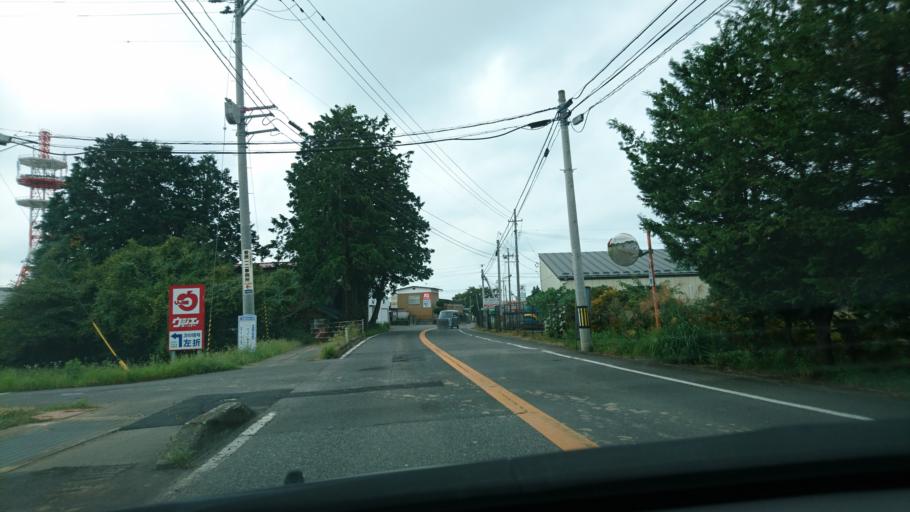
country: JP
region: Miyagi
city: Furukawa
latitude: 38.7369
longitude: 141.0331
